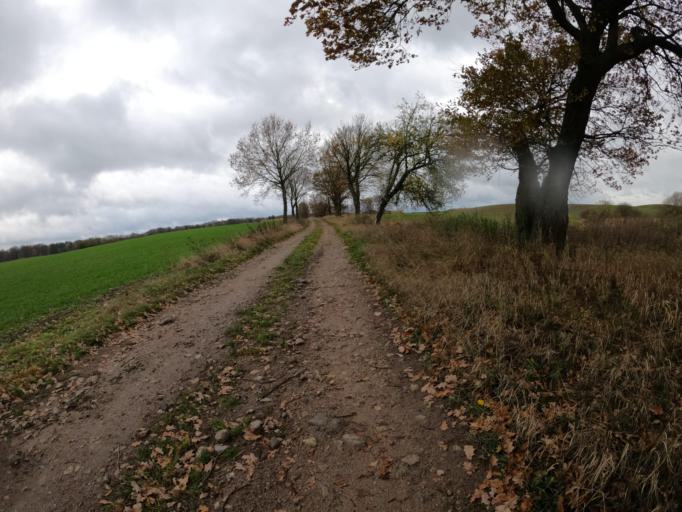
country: PL
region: West Pomeranian Voivodeship
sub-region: Powiat walecki
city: Tuczno
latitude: 53.2577
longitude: 16.2319
